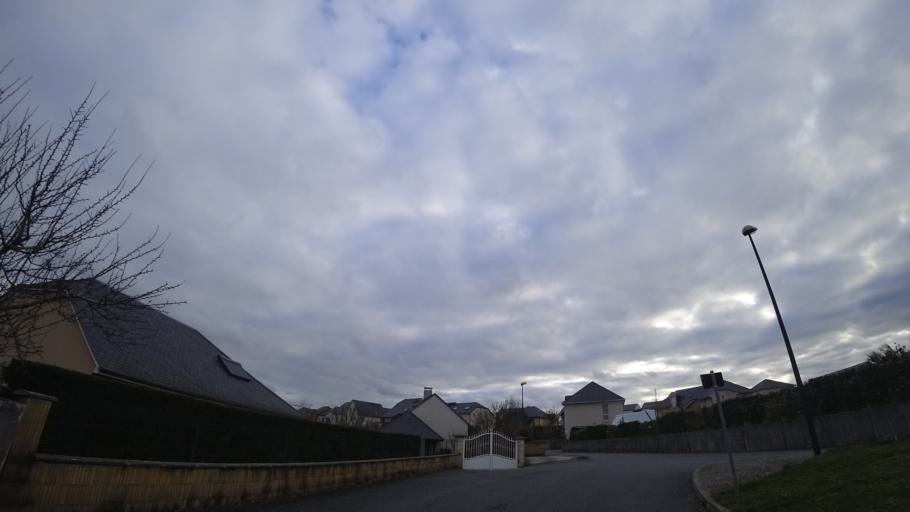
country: FR
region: Midi-Pyrenees
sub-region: Departement de l'Aveyron
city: Le Monastere
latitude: 44.3381
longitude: 2.5726
